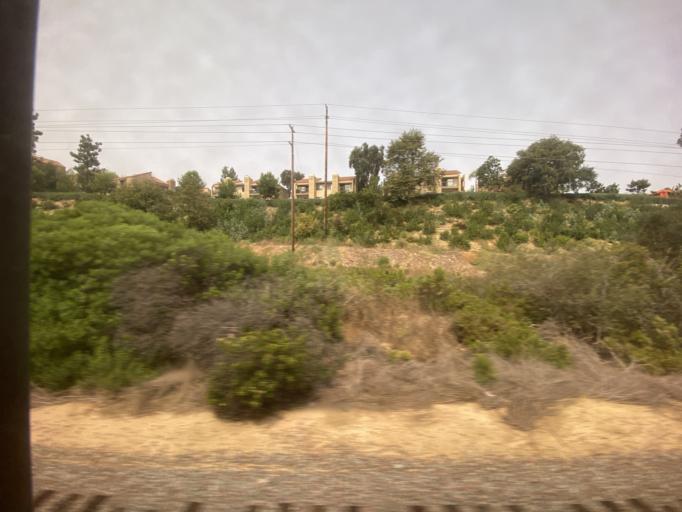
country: US
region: California
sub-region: San Diego County
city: La Jolla
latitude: 32.8624
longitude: -117.2094
